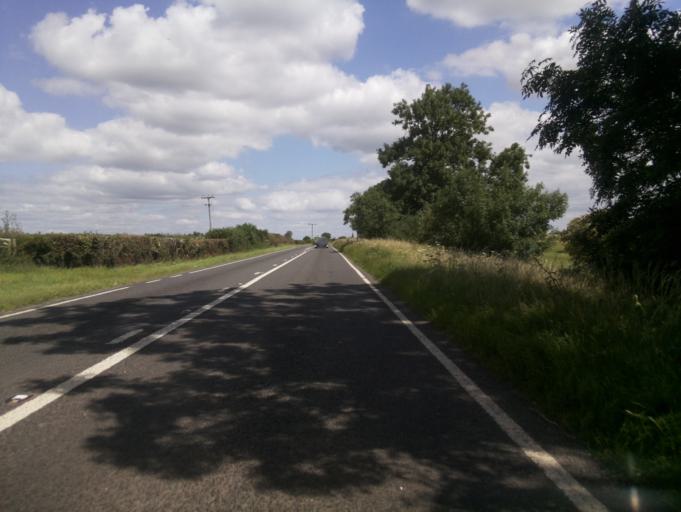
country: GB
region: England
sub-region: Buckinghamshire
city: Winslow
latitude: 51.8856
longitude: -0.8396
